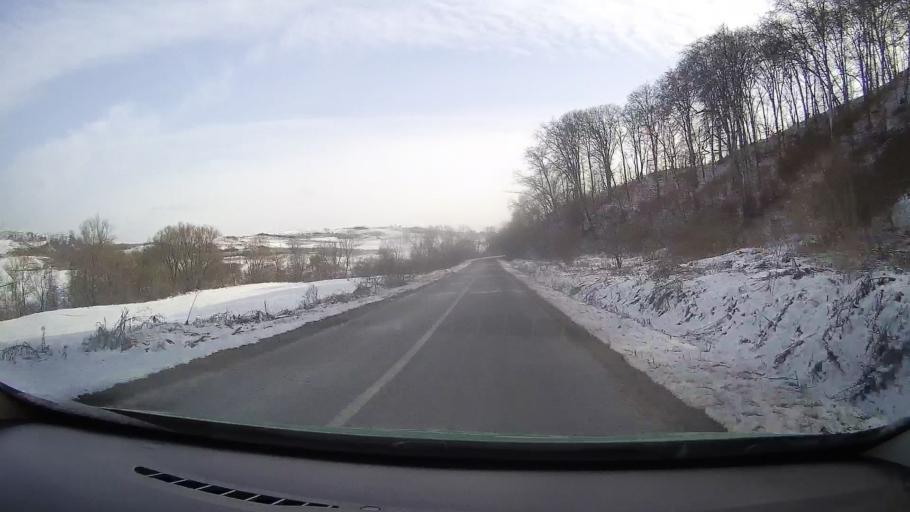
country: RO
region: Mures
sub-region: Comuna Apold
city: Saes
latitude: 46.1712
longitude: 24.7567
